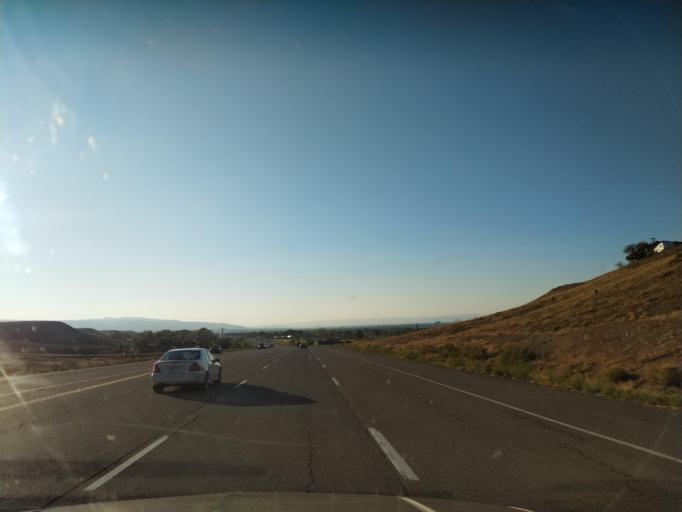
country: US
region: Colorado
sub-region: Mesa County
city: Fruitvale
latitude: 39.0178
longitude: -108.4807
